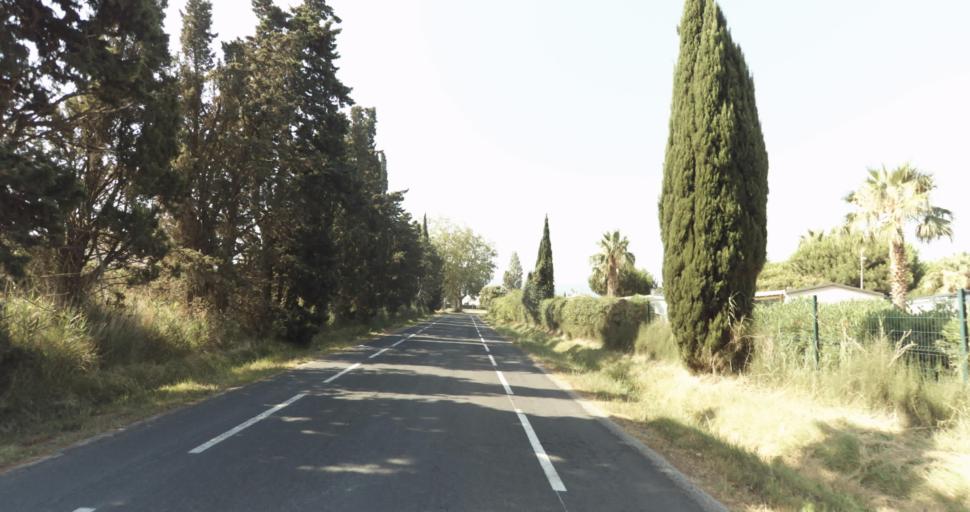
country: FR
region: Languedoc-Roussillon
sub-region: Departement des Pyrenees-Orientales
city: Latour-Bas-Elne
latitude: 42.6268
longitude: 3.0028
